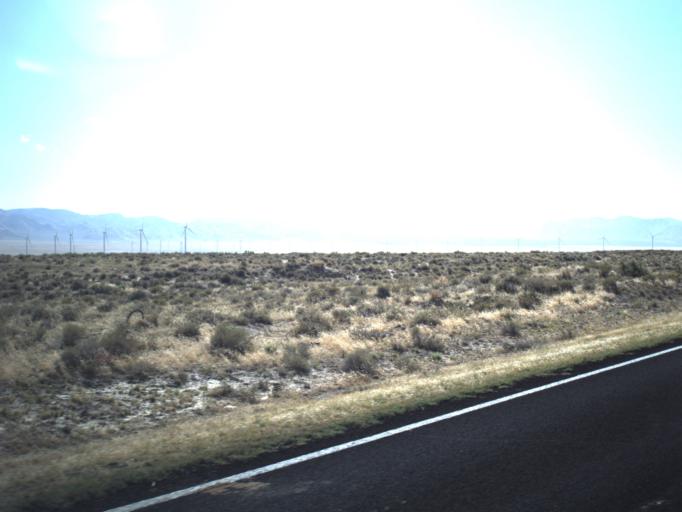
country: US
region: Utah
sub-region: Beaver County
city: Milford
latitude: 38.5462
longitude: -112.9912
